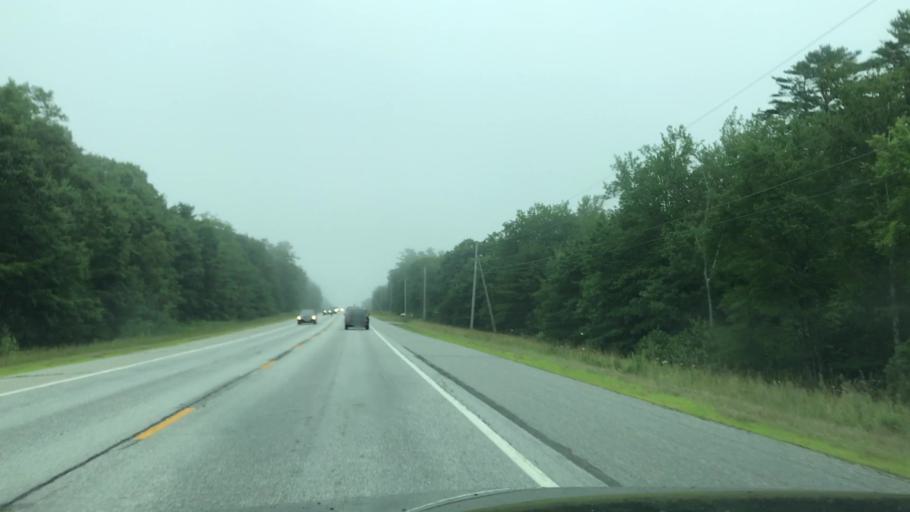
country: US
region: Maine
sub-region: Lincoln County
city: Nobleboro
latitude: 44.0813
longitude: -69.4746
